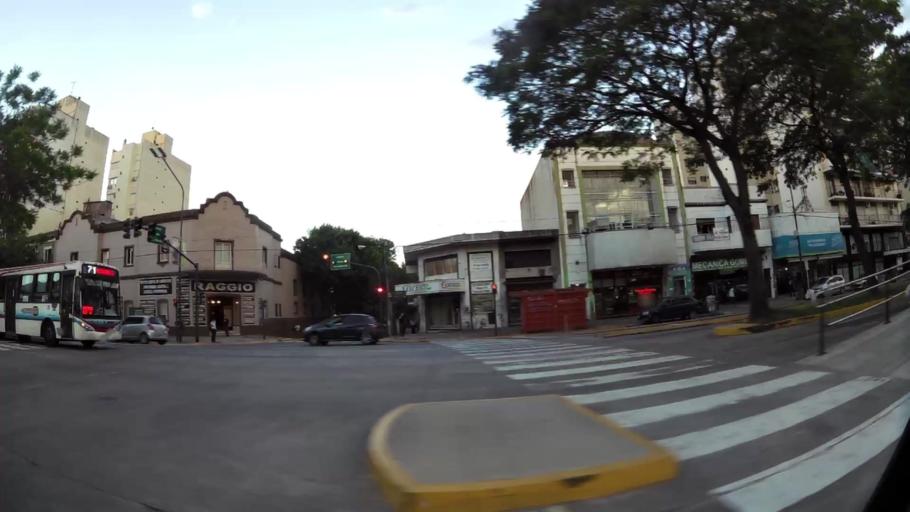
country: AR
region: Buenos Aires
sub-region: Partido de Vicente Lopez
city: Olivos
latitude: -34.5299
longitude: -58.4806
